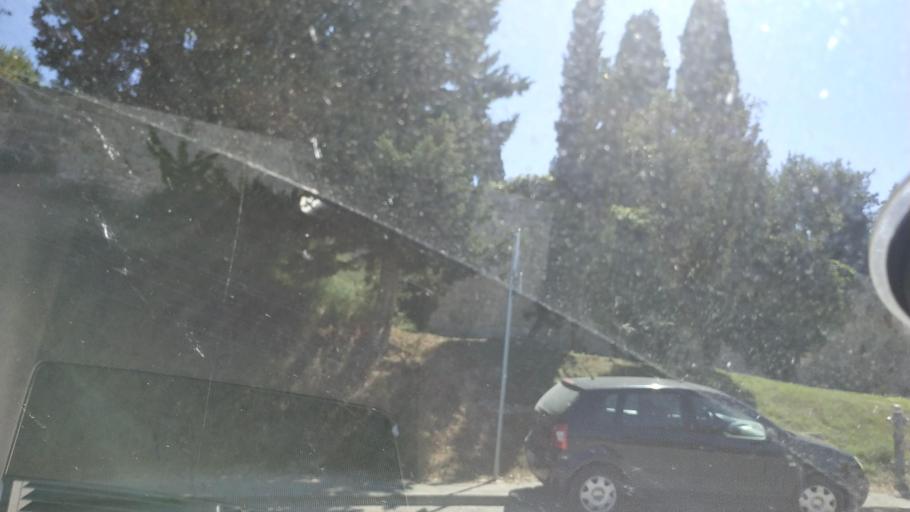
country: HR
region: Splitsko-Dalmatinska
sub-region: Grad Split
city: Split
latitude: 43.5016
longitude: 16.4259
